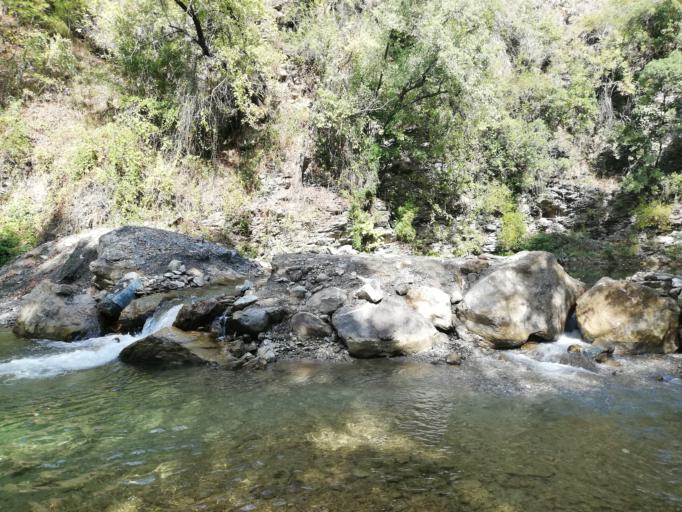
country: TR
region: Antalya
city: Guzelbag
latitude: 36.6689
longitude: 31.8908
